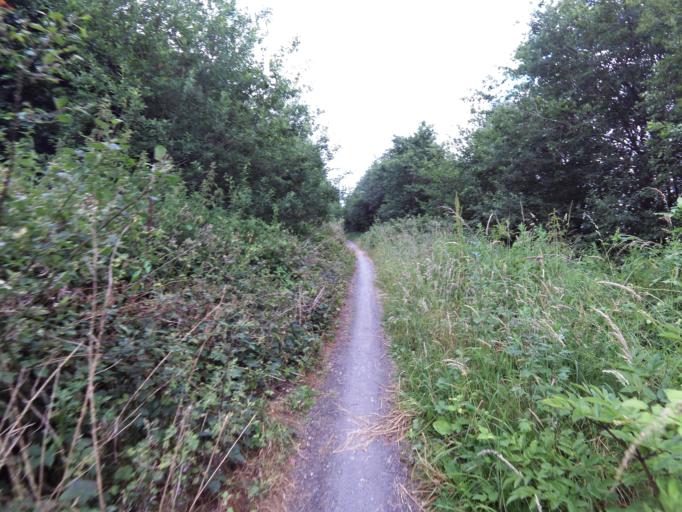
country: GB
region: England
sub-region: Norfolk
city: Ditchingham
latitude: 52.4674
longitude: 1.4615
